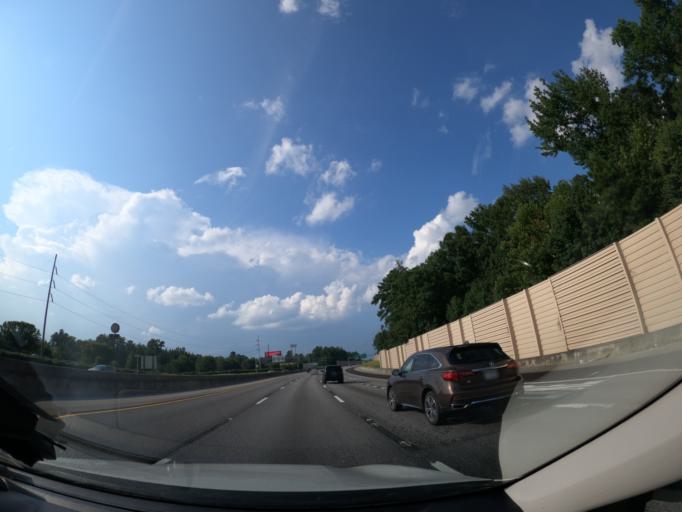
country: US
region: Georgia
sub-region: Columbia County
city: Martinez
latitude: 33.4743
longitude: -82.0862
